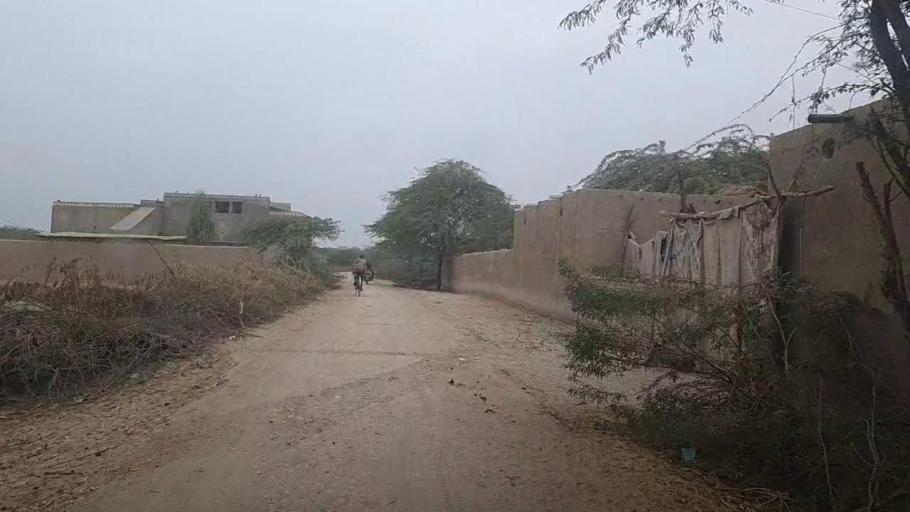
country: PK
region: Sindh
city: Gambat
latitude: 27.3513
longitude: 68.6001
